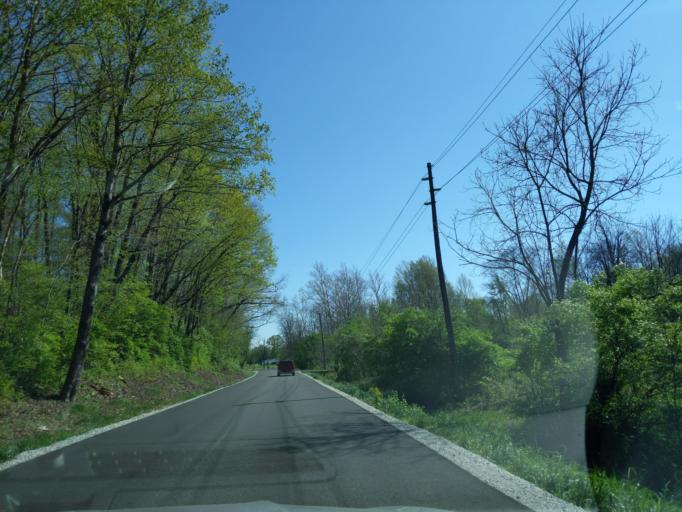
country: US
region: Indiana
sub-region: Decatur County
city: Greensburg
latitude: 39.3053
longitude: -85.4908
